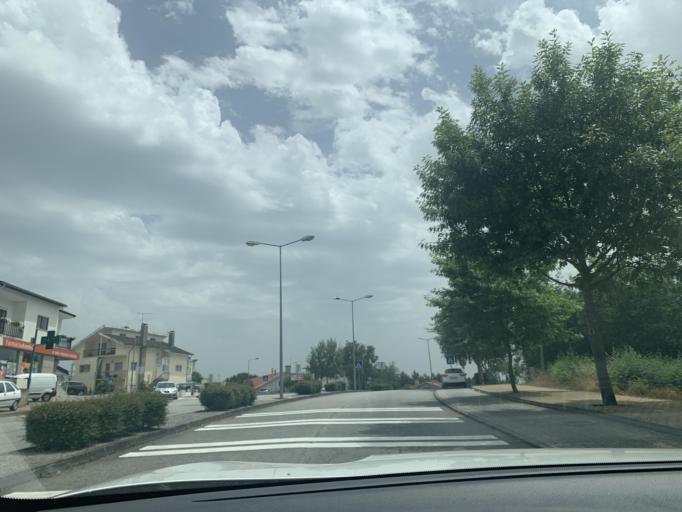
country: PT
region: Viseu
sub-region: Mangualde
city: Mangualde
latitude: 40.5960
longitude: -7.7578
